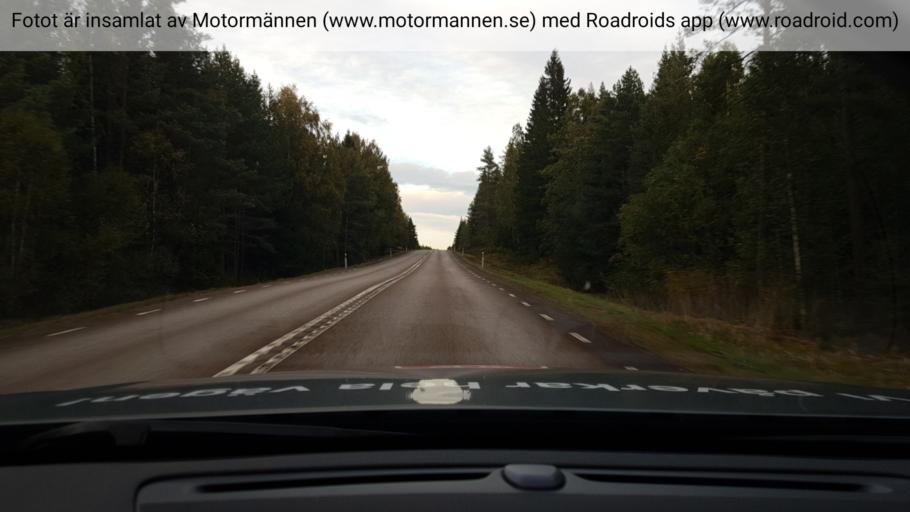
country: SE
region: Vaestra Goetaland
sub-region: Amals Kommun
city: Amal
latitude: 59.0595
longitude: 12.5373
